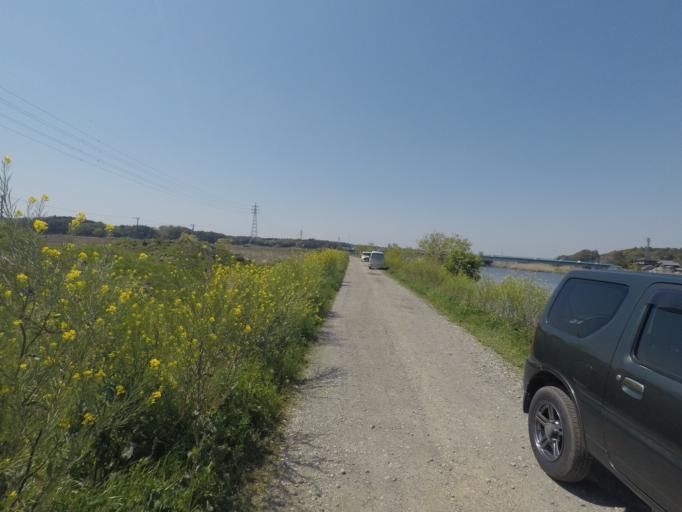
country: JP
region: Ibaraki
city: Ushiku
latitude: 35.9529
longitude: 140.1045
